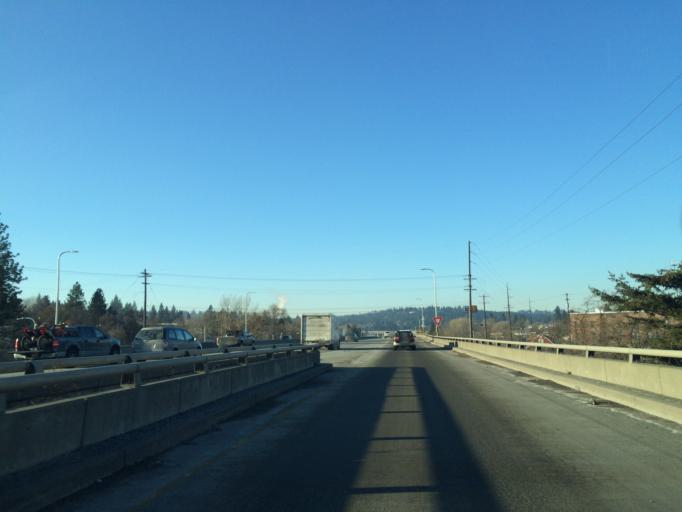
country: US
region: Washington
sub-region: Spokane County
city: Spokane
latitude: 47.6527
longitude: -117.4333
